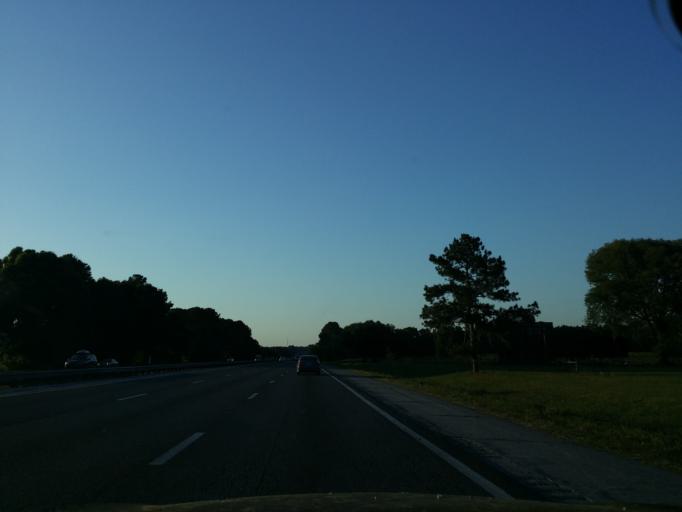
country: US
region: Florida
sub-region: Alachua County
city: High Springs
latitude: 29.9196
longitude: -82.5554
